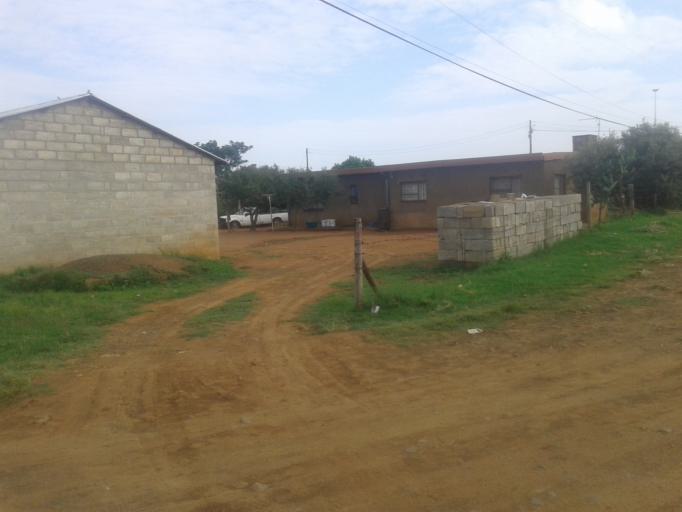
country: LS
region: Maseru
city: Maseru
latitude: -29.3021
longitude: 27.5284
